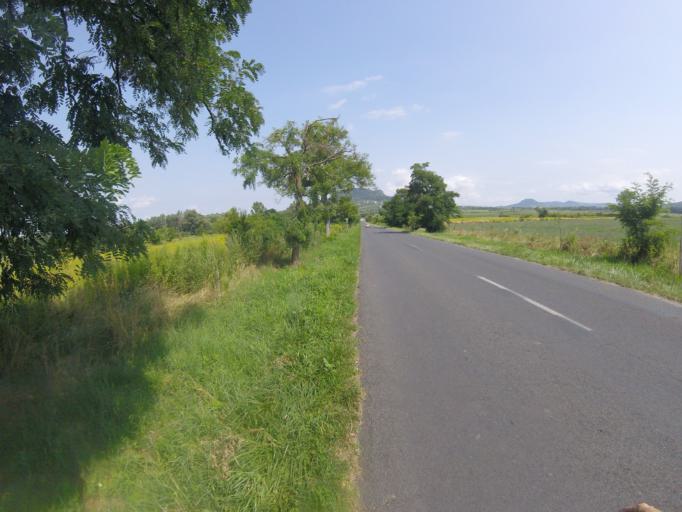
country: HU
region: Veszprem
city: Badacsonytomaj
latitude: 46.8122
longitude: 17.4476
